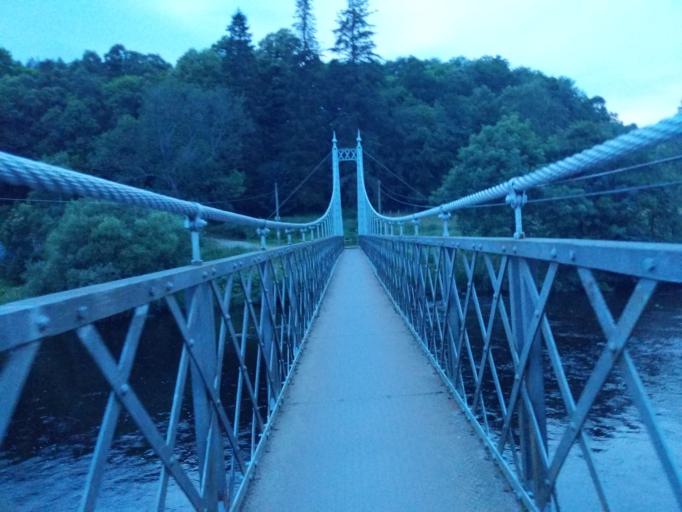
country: GB
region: Scotland
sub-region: Moray
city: Rothes
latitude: 57.4704
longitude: -3.2316
